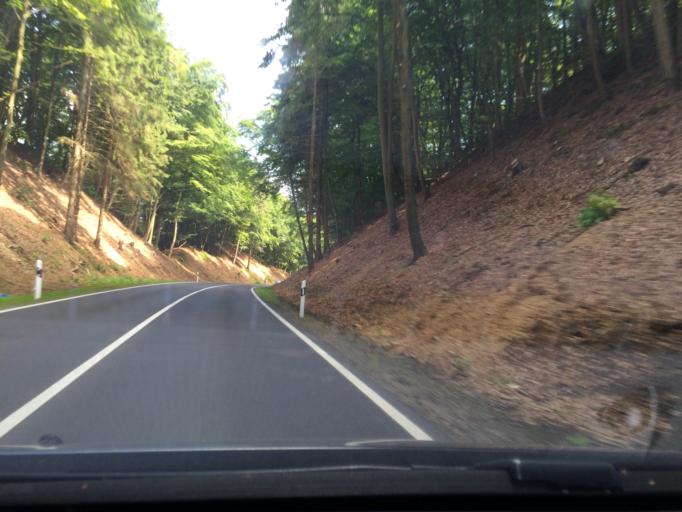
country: DE
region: Mecklenburg-Vorpommern
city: Ostseebad Binz
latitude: 54.4327
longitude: 13.5540
